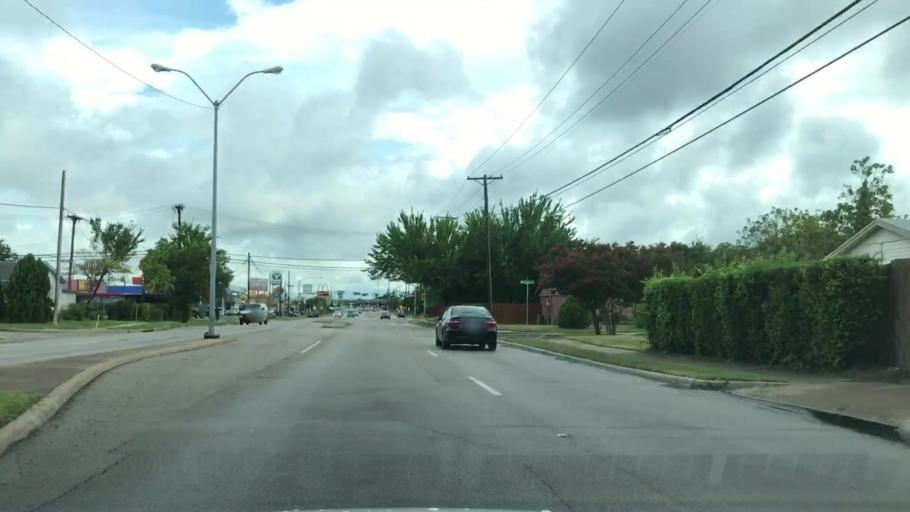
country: US
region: Texas
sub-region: Dallas County
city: Irving
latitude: 32.8437
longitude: -96.9765
